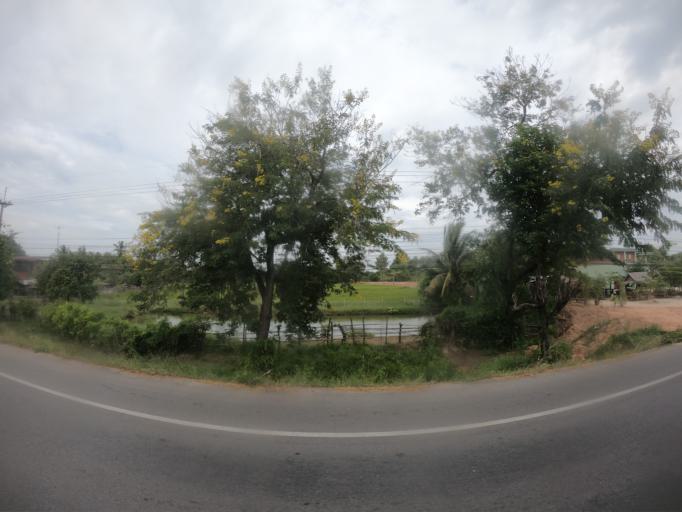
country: TH
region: Kalasin
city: Khong Chai
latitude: 16.1436
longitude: 103.4195
